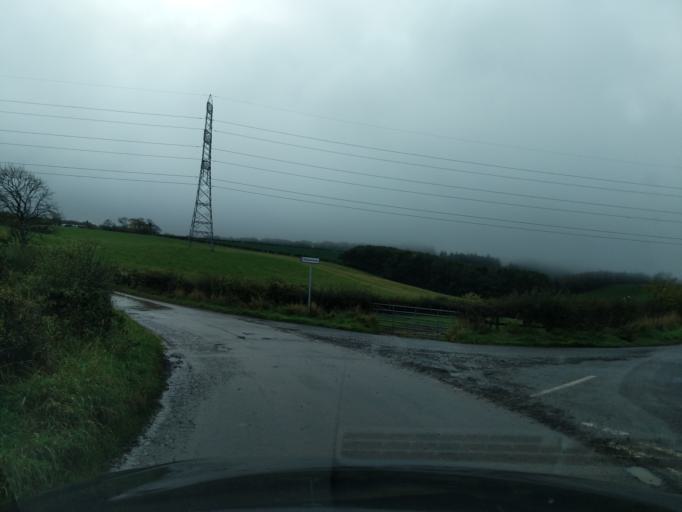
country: GB
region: Scotland
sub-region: East Lothian
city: Dunbar
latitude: 55.9423
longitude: -2.4057
